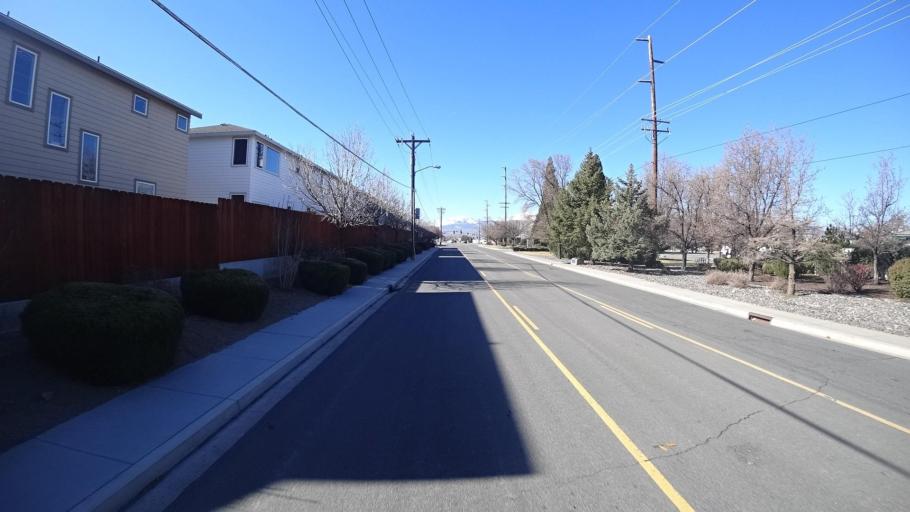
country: US
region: Nevada
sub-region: Washoe County
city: Sparks
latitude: 39.5003
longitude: -119.7509
